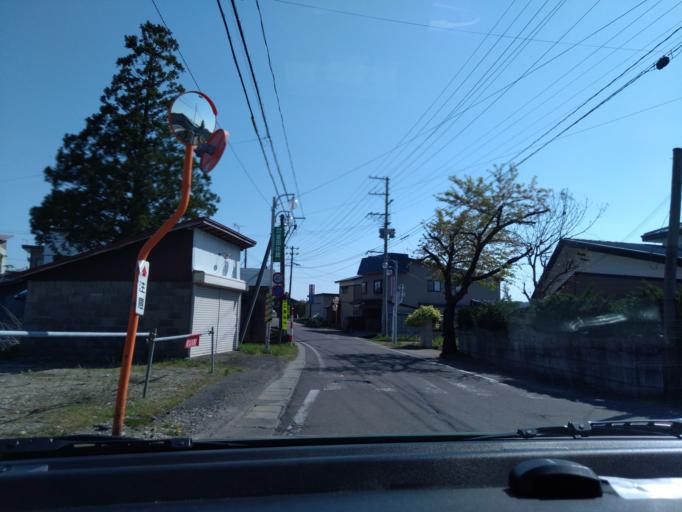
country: JP
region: Akita
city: Kakunodatemachi
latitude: 39.4978
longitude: 140.5942
